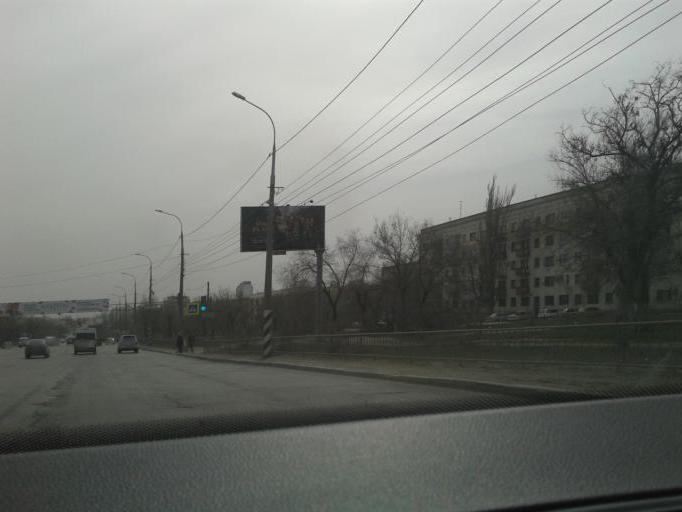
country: RU
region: Volgograd
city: Volgograd
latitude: 48.6622
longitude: 44.4392
